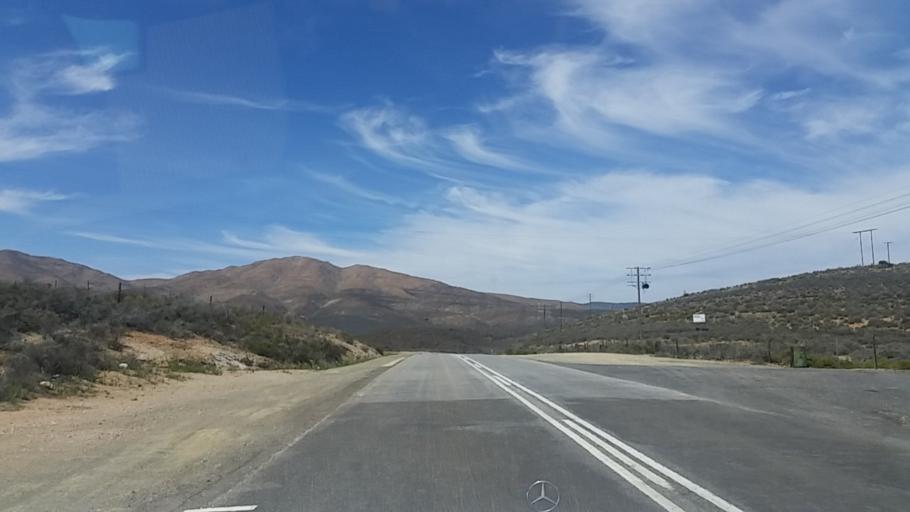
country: ZA
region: Western Cape
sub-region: Eden District Municipality
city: Knysna
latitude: -33.6341
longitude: 23.1288
